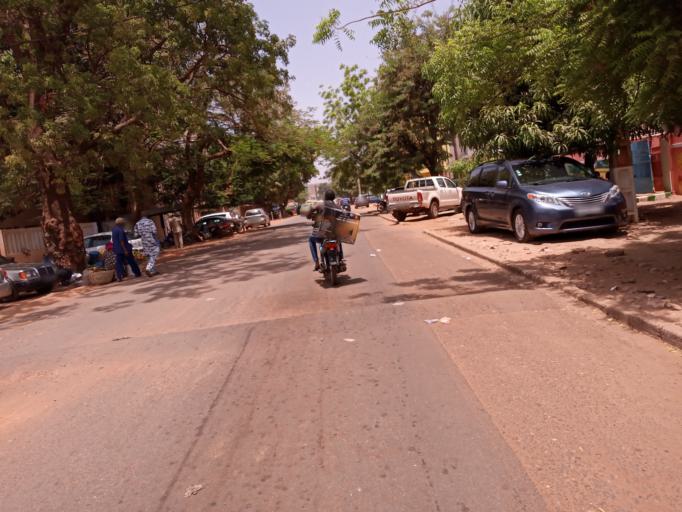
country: ML
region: Bamako
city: Bamako
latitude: 12.6347
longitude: -8.0005
